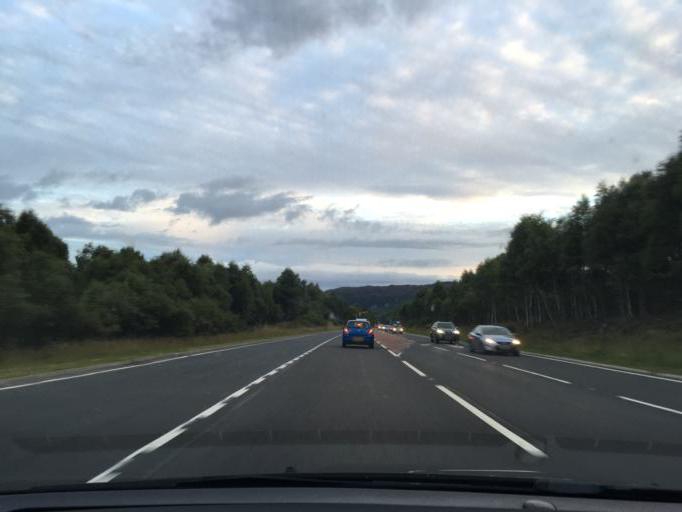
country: GB
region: Scotland
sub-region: Highland
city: Aviemore
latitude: 57.2149
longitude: -3.8239
